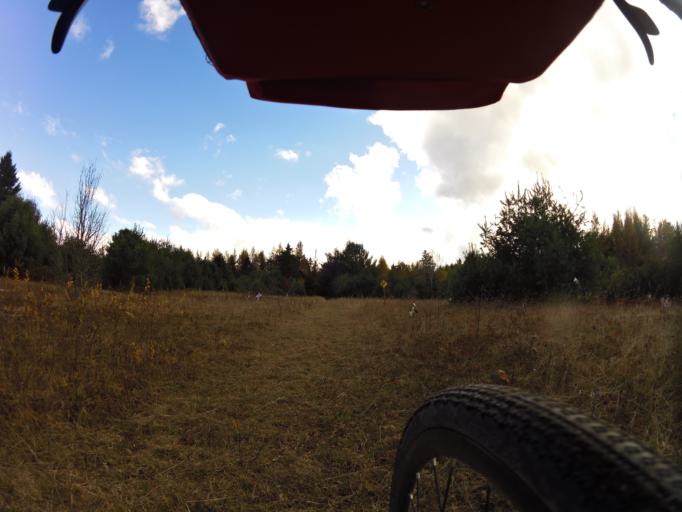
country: CA
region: Quebec
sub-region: Outaouais
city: Wakefield
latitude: 45.6803
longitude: -76.1216
